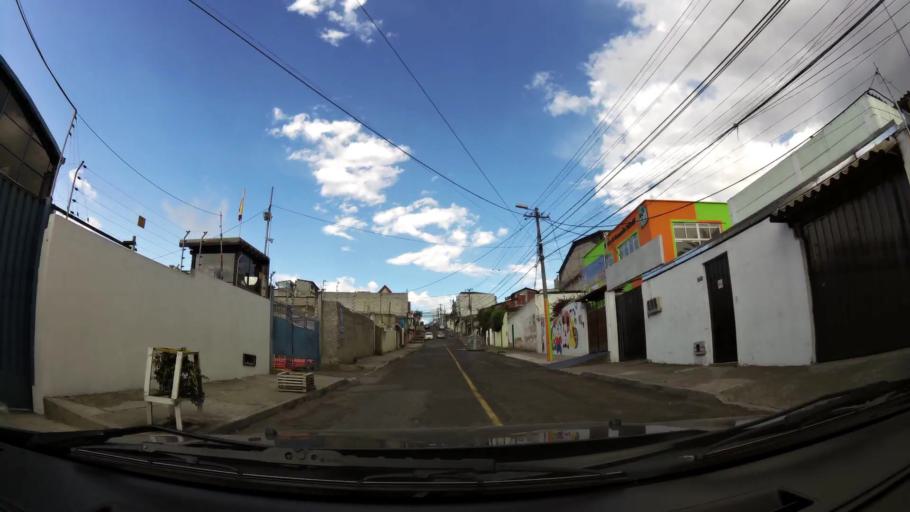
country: EC
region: Pichincha
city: Quito
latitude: -0.1212
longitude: -78.4874
